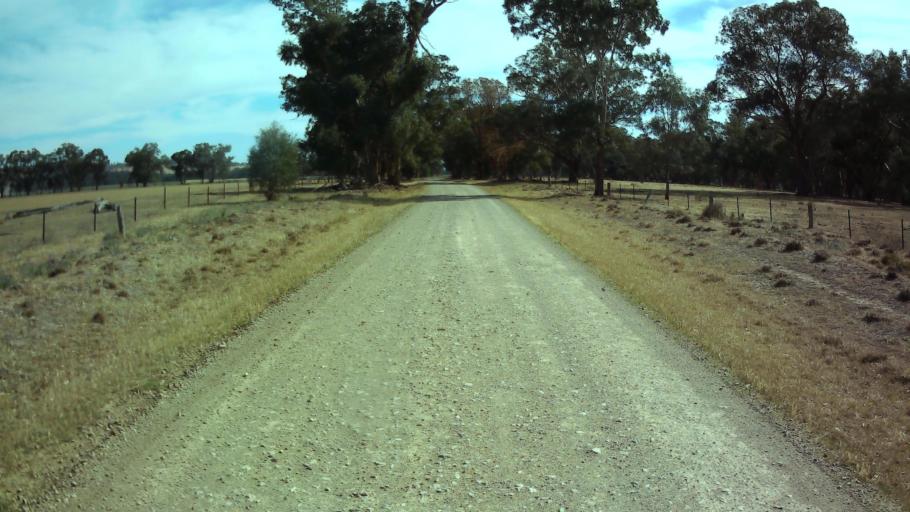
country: AU
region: New South Wales
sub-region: Weddin
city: Grenfell
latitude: -33.6904
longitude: 148.3042
